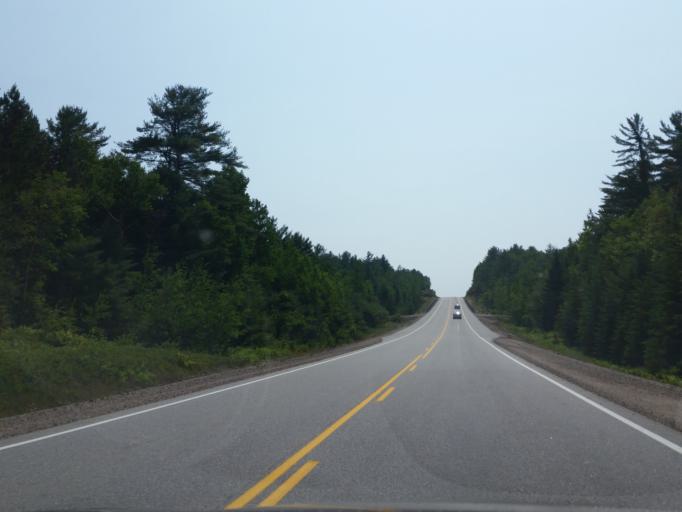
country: CA
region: Ontario
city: Mattawa
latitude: 46.2865
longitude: -78.5149
